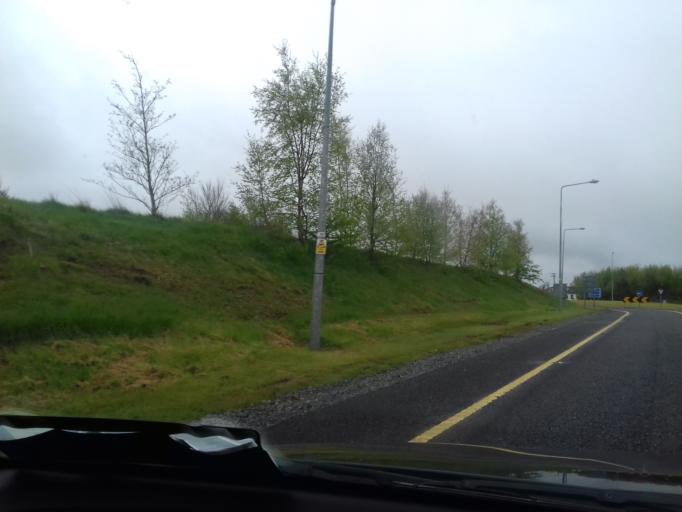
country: IE
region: Leinster
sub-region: Laois
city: Portlaoise
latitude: 53.0508
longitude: -7.2376
